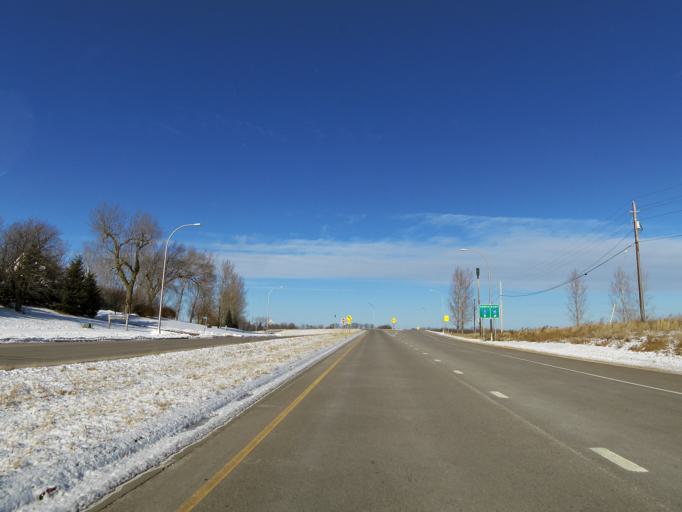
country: US
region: Minnesota
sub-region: Scott County
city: Shakopee
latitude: 44.7430
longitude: -93.4997
